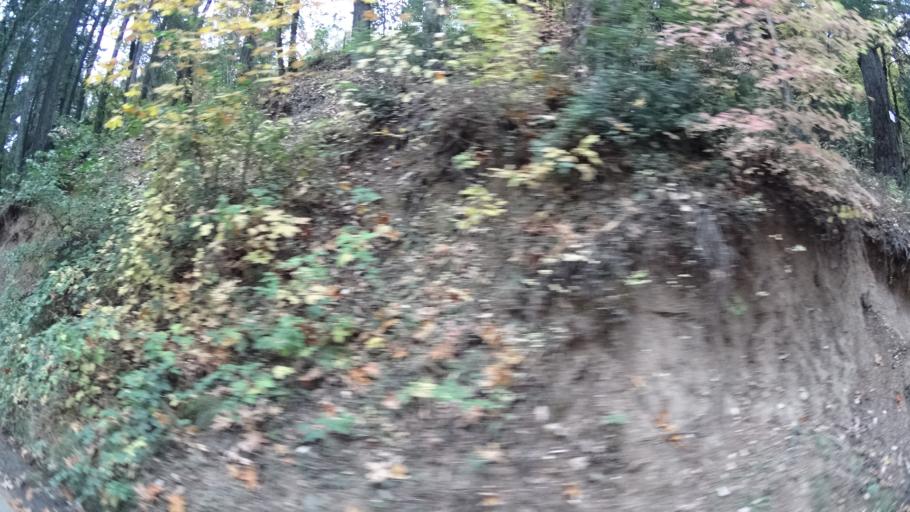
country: US
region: California
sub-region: Siskiyou County
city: Happy Camp
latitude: 41.8006
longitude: -123.3819
